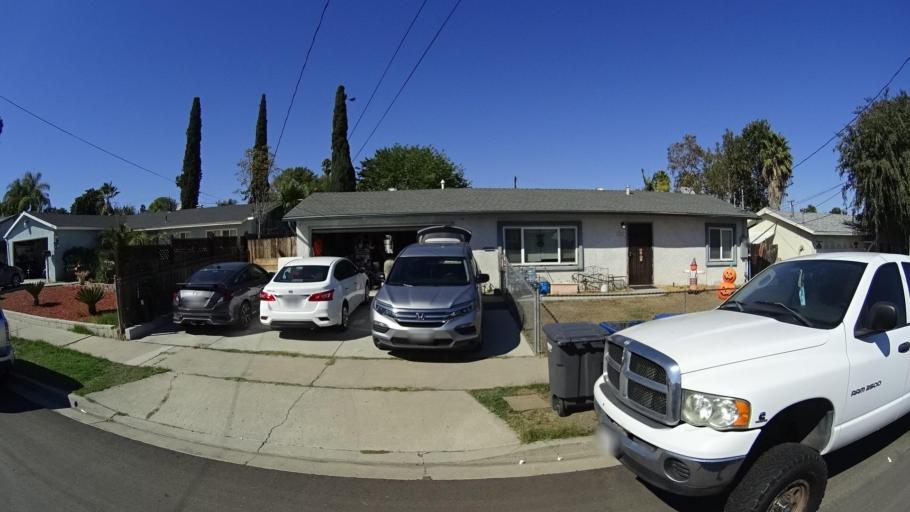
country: US
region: California
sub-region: San Diego County
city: La Presa
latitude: 32.7060
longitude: -117.0158
